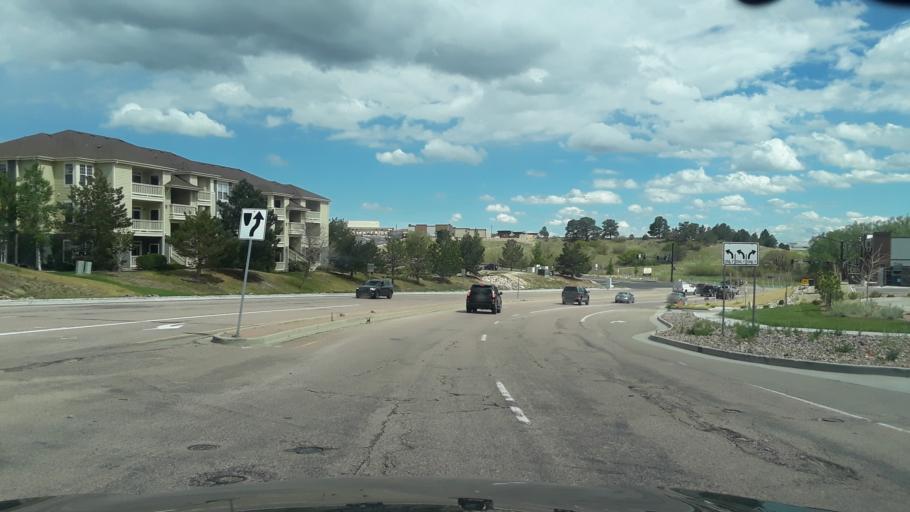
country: US
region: Colorado
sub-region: El Paso County
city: Gleneagle
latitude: 39.0297
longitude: -104.8290
